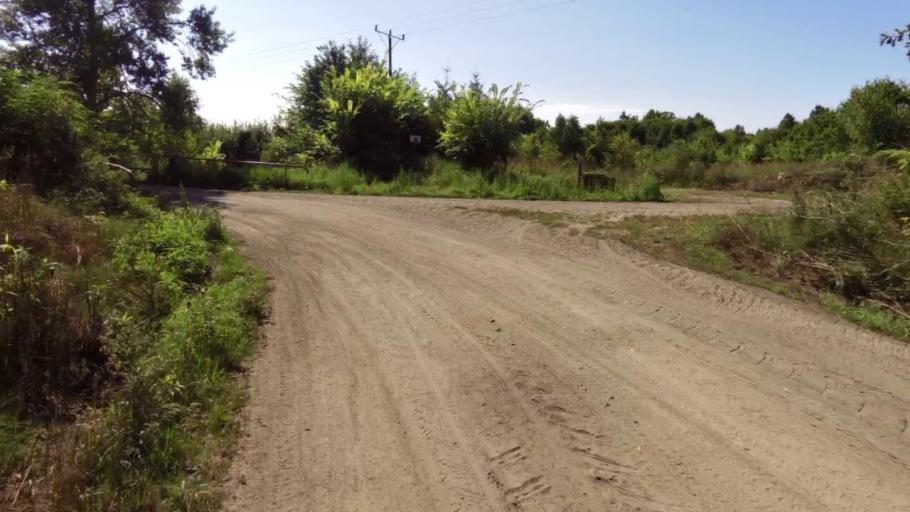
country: PL
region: West Pomeranian Voivodeship
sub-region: Powiat drawski
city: Zlocieniec
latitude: 53.5205
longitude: 16.0484
